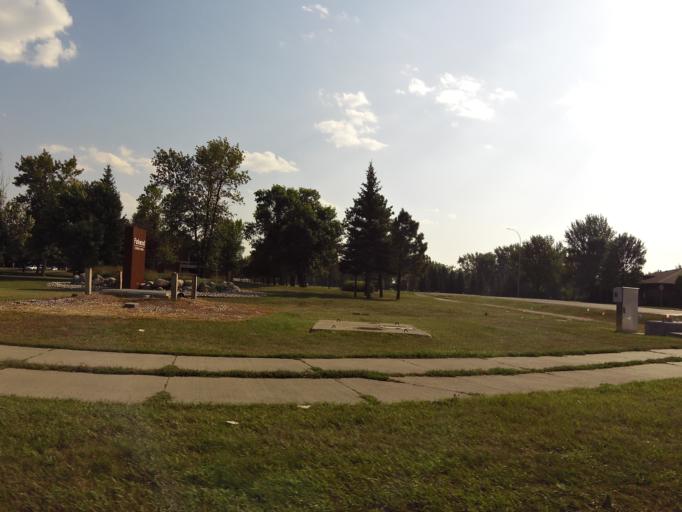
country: US
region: North Dakota
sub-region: Grand Forks County
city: Grand Forks
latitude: 47.9164
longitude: -97.0706
